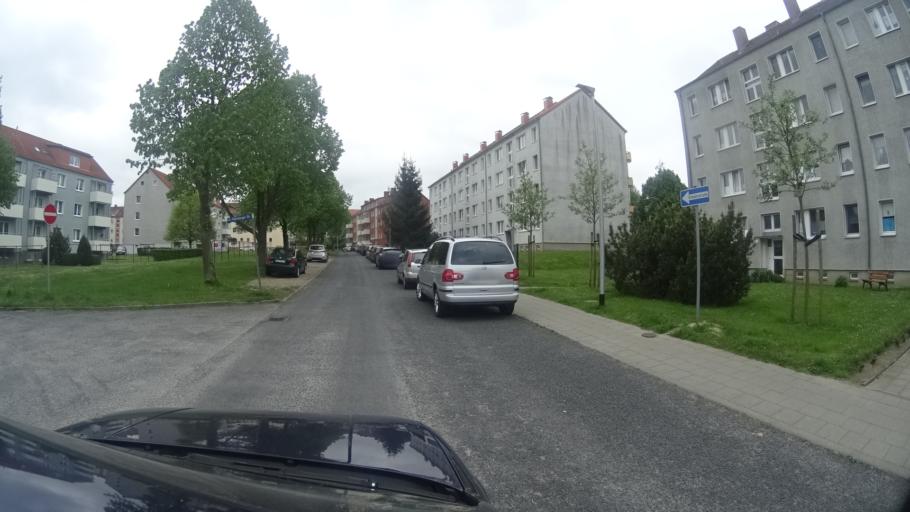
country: DE
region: Mecklenburg-Vorpommern
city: Ribnitz-Damgarten
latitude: 54.2418
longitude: 12.4108
